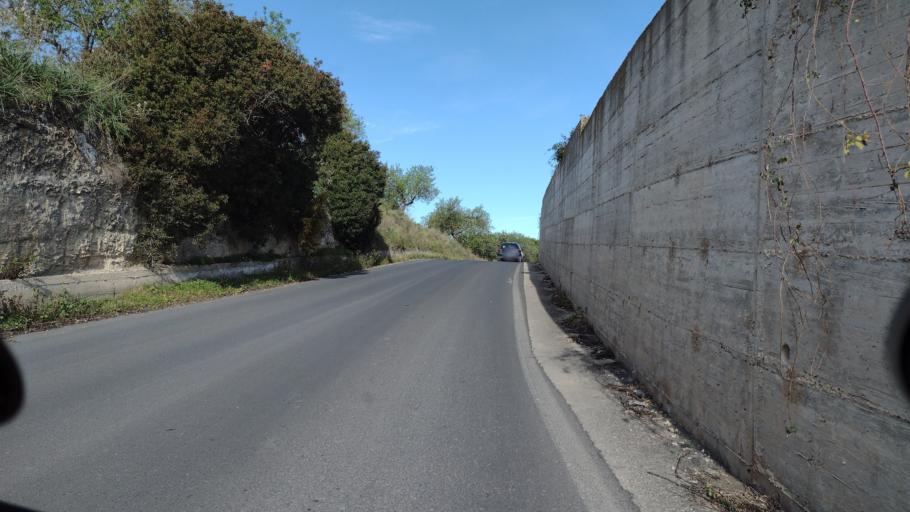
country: IT
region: Sicily
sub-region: Provincia di Siracusa
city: Noto
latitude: 36.8772
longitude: 15.0915
